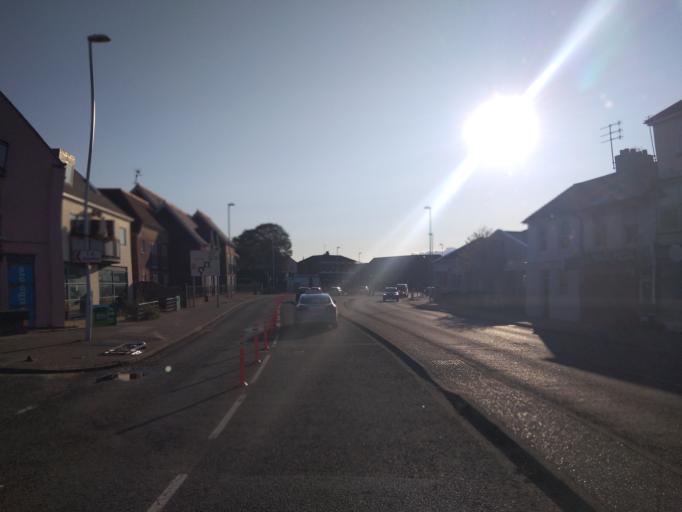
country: GB
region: England
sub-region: West Sussex
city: Worthing
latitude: 50.8153
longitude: -0.3703
